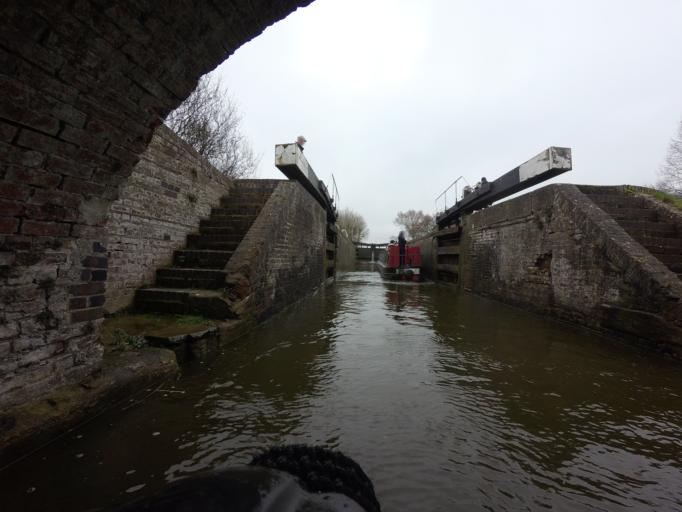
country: GB
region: England
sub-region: Buckinghamshire
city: Cheddington
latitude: 51.8557
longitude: -0.6457
